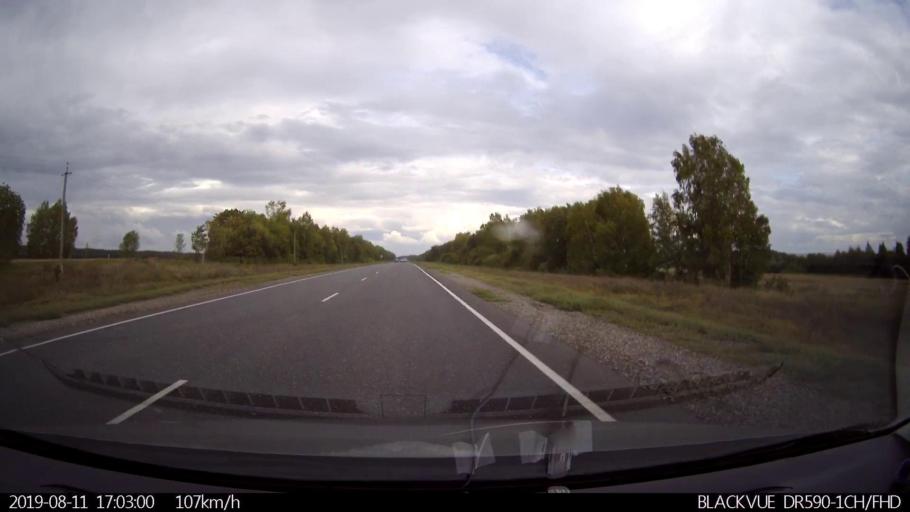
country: RU
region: Ulyanovsk
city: Mayna
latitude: 54.3044
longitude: 47.7287
